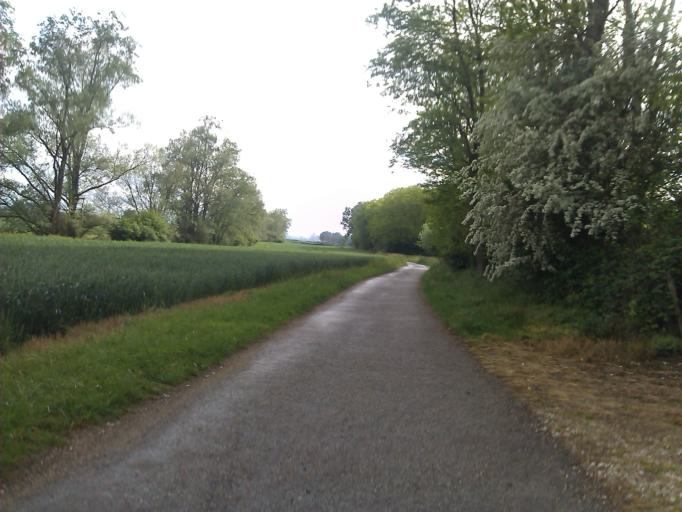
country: FR
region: Bourgogne
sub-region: Departement de Saone-et-Loire
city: Sassenay
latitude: 46.8214
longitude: 4.9165
